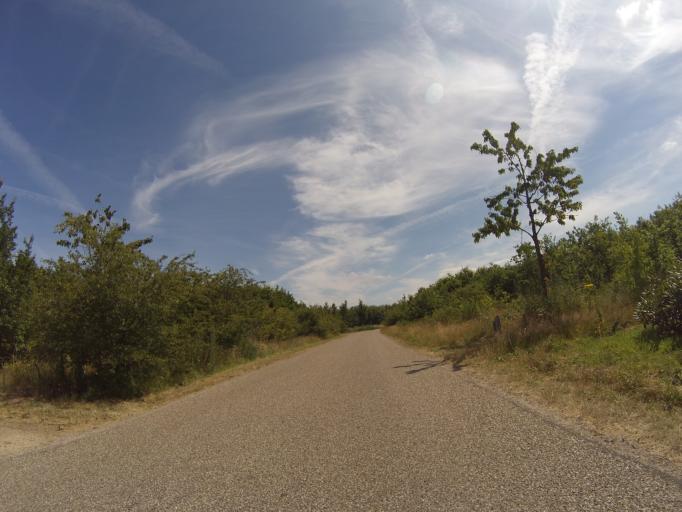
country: NL
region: Gelderland
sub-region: Gemeente Ermelo
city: Horst
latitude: 52.3233
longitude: 5.5792
